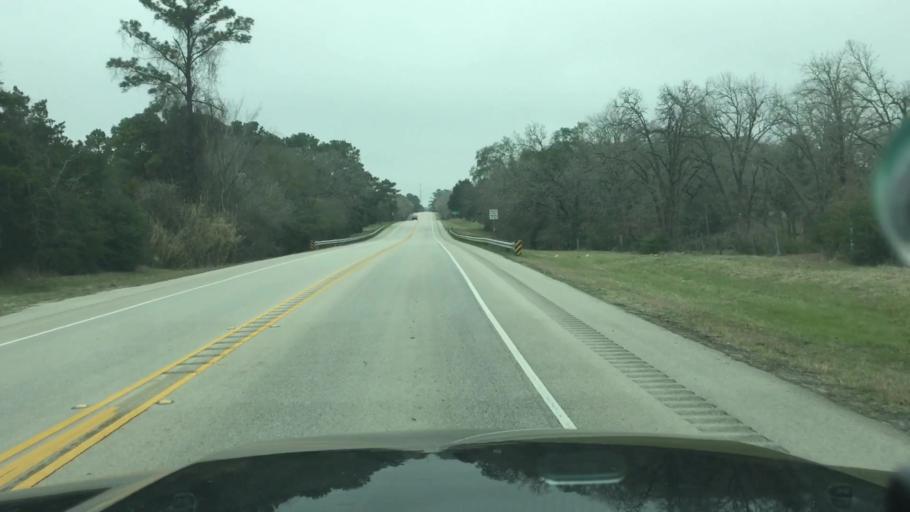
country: US
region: Texas
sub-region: Fayette County
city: La Grange
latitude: 30.0000
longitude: -96.8917
